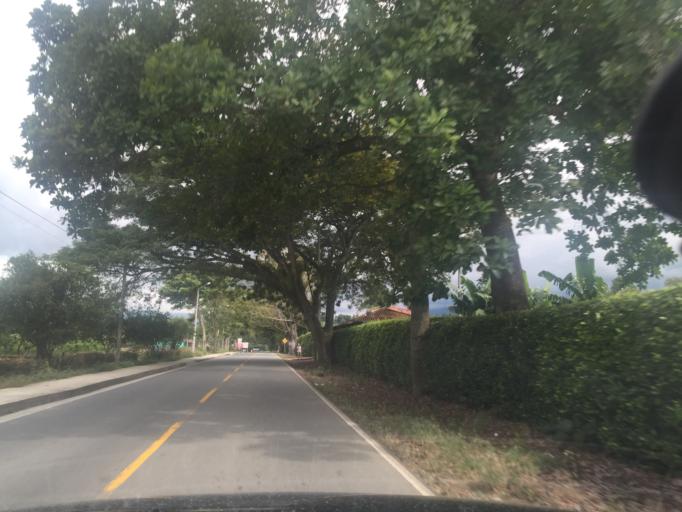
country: CO
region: Valle del Cauca
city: Caicedonia
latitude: 4.3422
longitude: -75.8495
